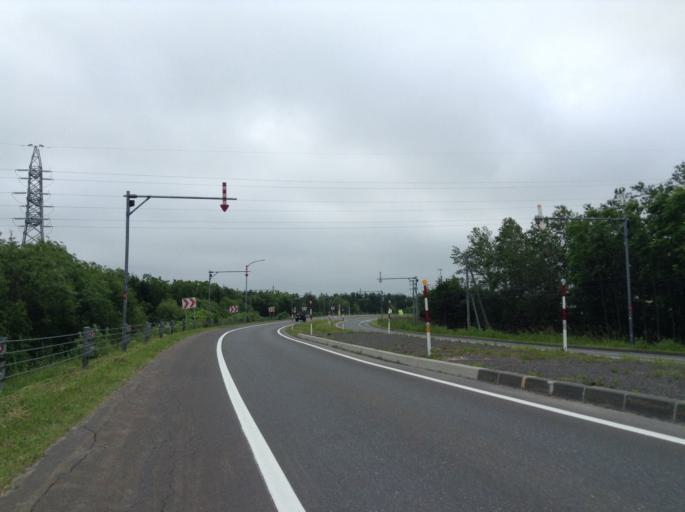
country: JP
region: Hokkaido
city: Wakkanai
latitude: 45.3694
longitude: 141.7258
